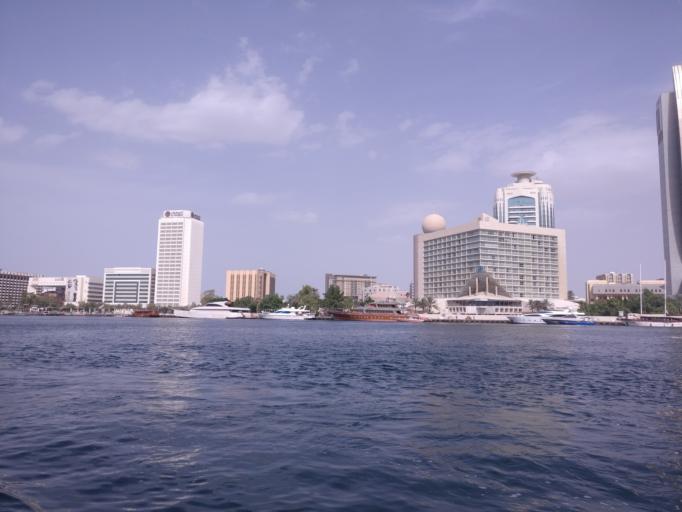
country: AE
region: Ash Shariqah
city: Sharjah
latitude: 25.2594
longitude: 55.3118
